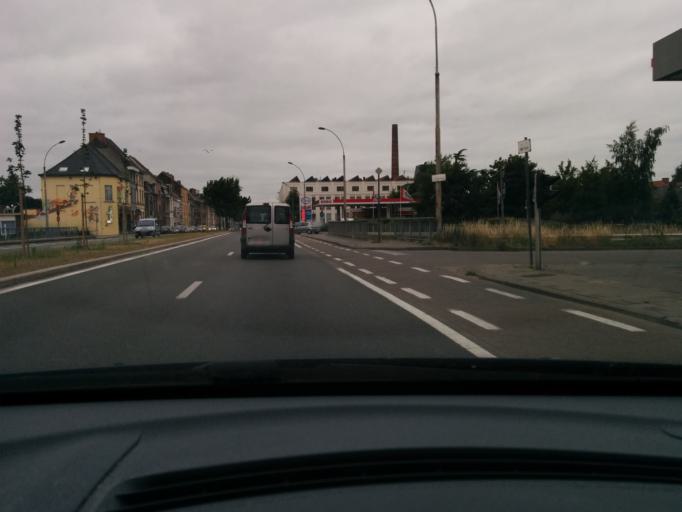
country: BE
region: Flanders
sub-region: Provincie Oost-Vlaanderen
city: Gent
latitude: 51.0532
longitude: 3.6989
